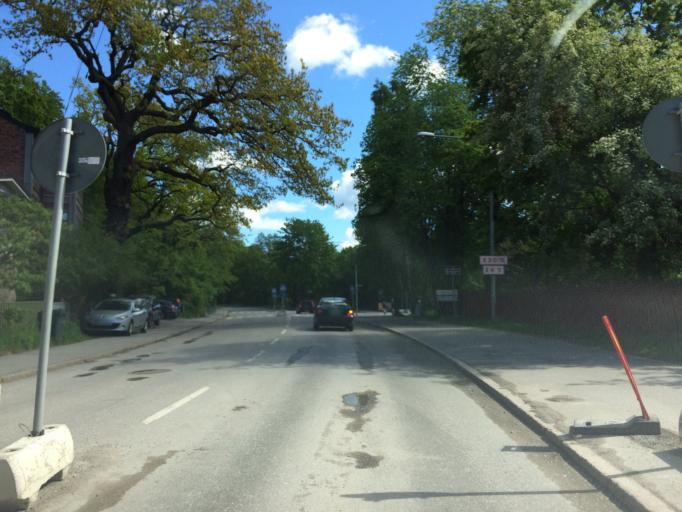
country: SE
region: Stockholm
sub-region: Stockholms Kommun
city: Arsta
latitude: 59.3136
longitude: 18.0091
